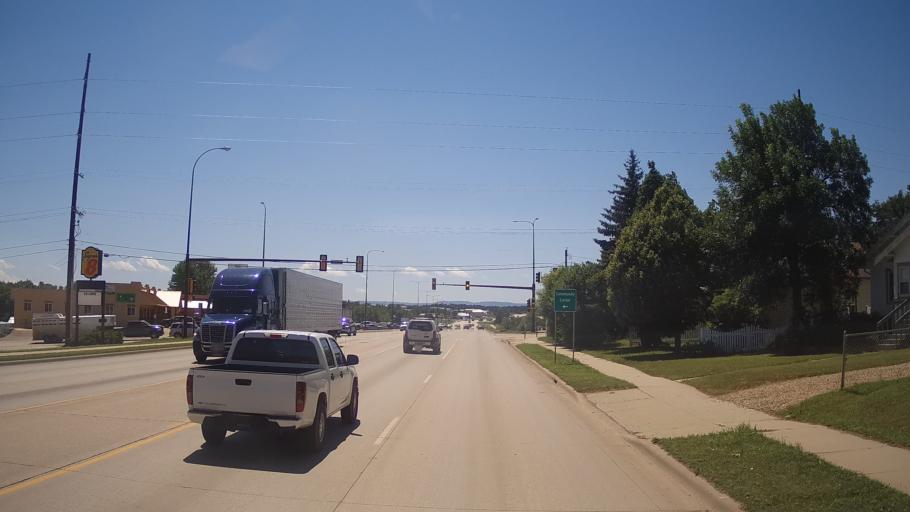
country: US
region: South Dakota
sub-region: Butte County
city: Belle Fourche
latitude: 44.6635
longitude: -103.8542
